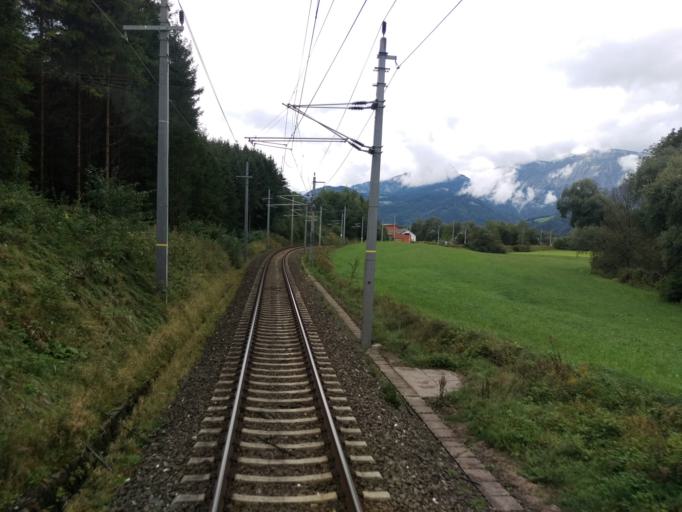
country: AT
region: Styria
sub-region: Politischer Bezirk Liezen
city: Liezen
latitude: 47.5507
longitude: 14.2615
